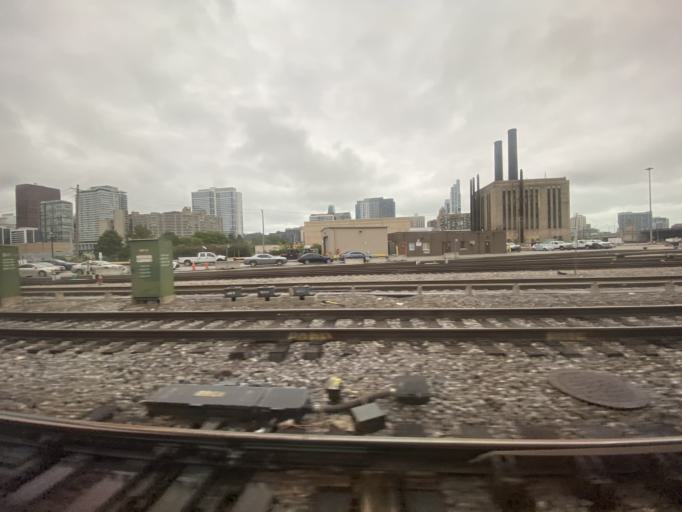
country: US
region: Illinois
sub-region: Cook County
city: Chicago
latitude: 41.8690
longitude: -87.6374
